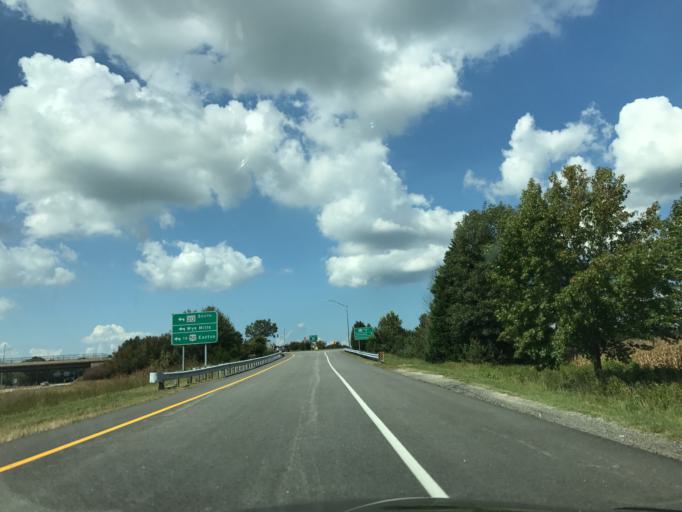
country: US
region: Maryland
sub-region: Queen Anne's County
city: Centreville
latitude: 39.0152
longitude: -76.0735
